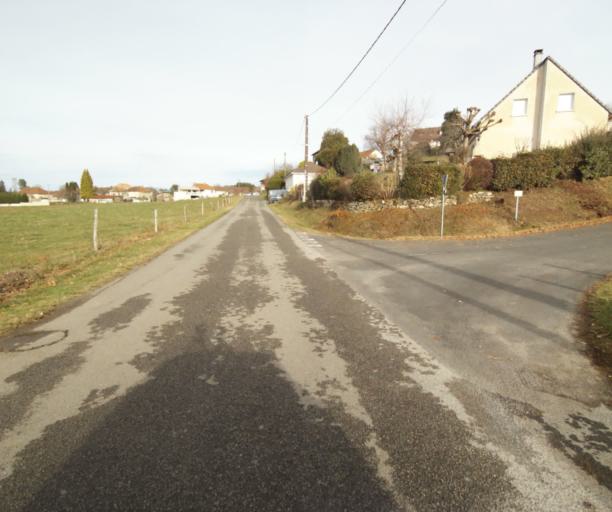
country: FR
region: Limousin
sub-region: Departement de la Correze
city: Saint-Mexant
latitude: 45.2671
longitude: 1.6789
